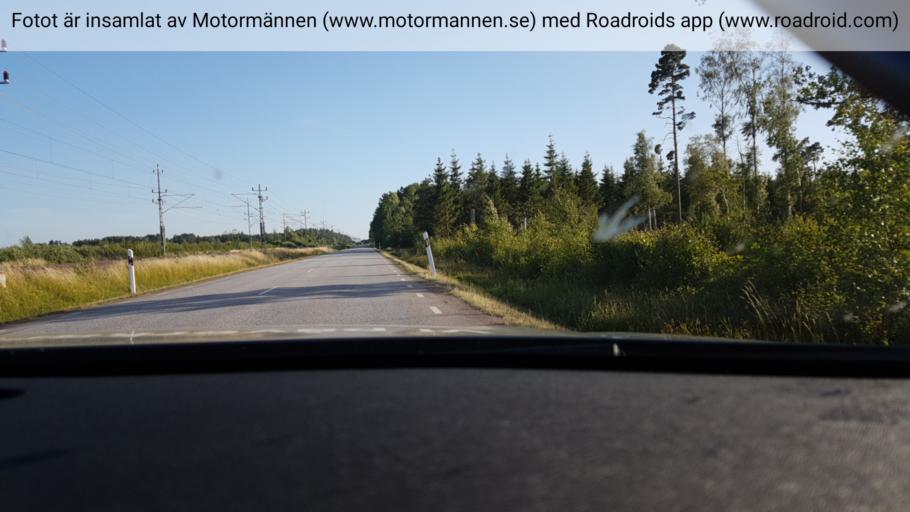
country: SE
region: Vaestra Goetaland
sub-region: Toreboda Kommun
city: Toereboda
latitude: 58.6806
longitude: 14.1044
